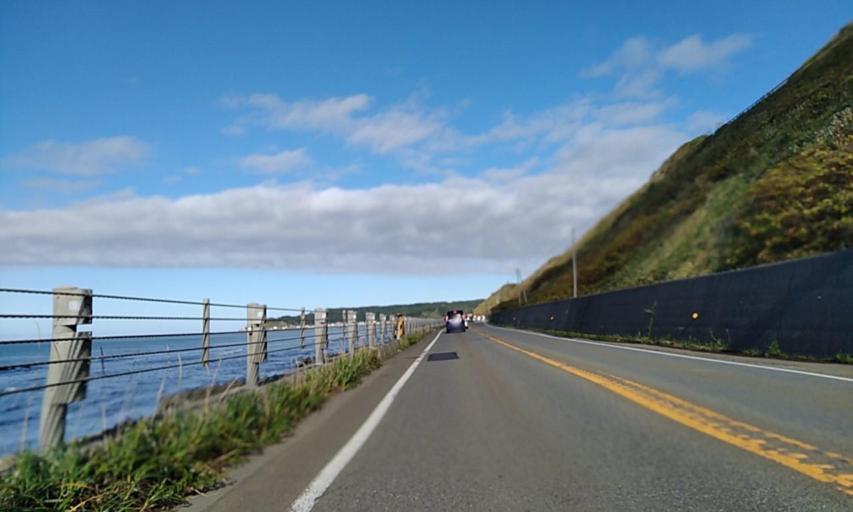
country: JP
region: Hokkaido
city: Shizunai-furukawacho
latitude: 42.2606
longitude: 142.5216
